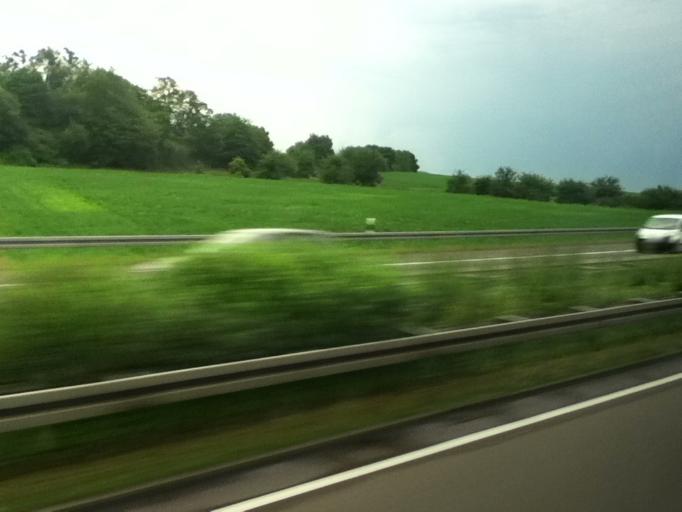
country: DE
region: Hesse
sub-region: Regierungsbezirk Giessen
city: Alsfeld
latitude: 50.7543
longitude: 9.3051
